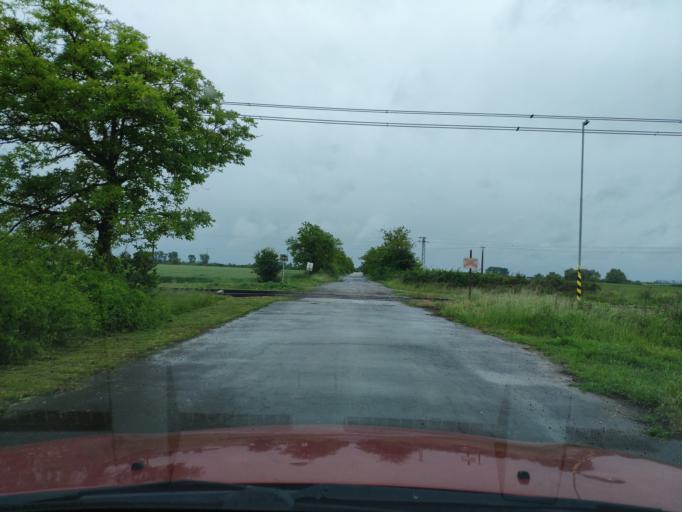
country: SK
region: Kosicky
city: Cierna nad Tisou
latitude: 48.4215
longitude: 22.0554
